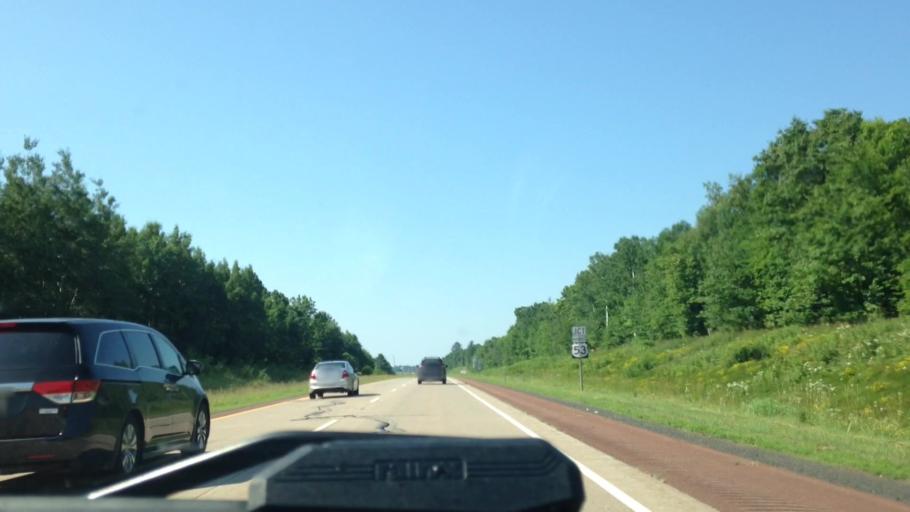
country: US
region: Wisconsin
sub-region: Douglas County
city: Lake Nebagamon
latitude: 46.3860
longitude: -91.8209
